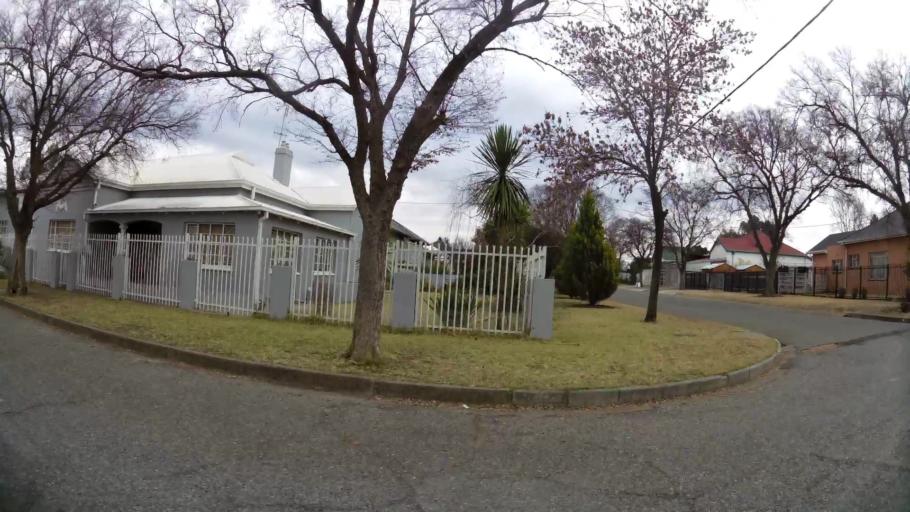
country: ZA
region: Orange Free State
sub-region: Fezile Dabi District Municipality
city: Kroonstad
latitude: -27.6552
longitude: 27.2436
